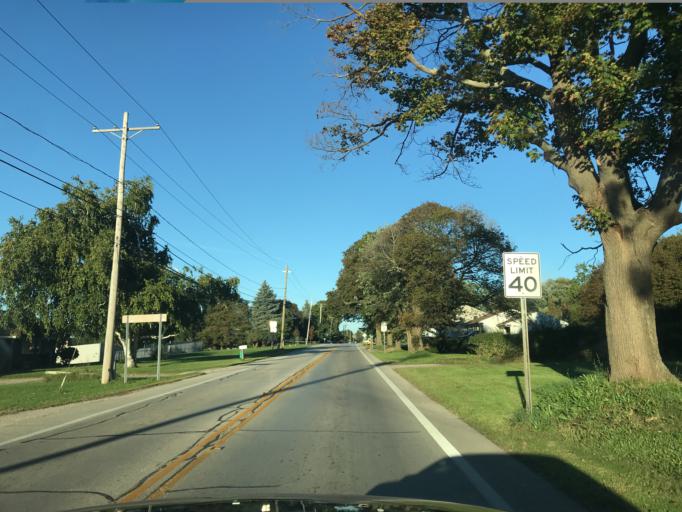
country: US
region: Ohio
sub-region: Ashtabula County
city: Edgewood
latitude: 41.8608
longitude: -80.7695
